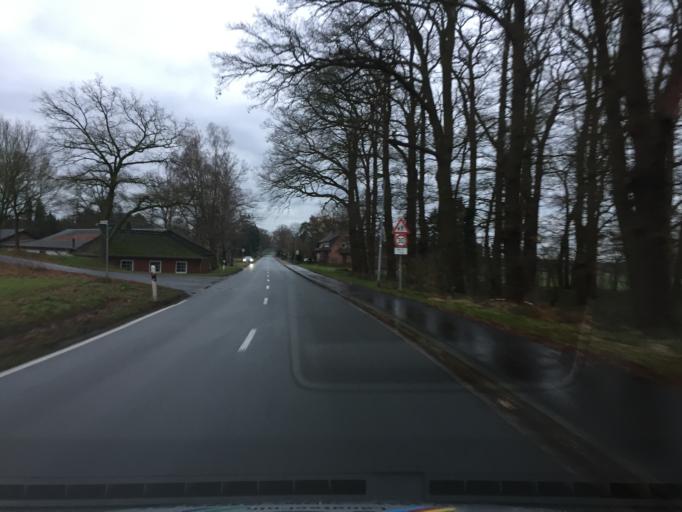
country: DE
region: Lower Saxony
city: Borstel
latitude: 52.6634
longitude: 8.9767
